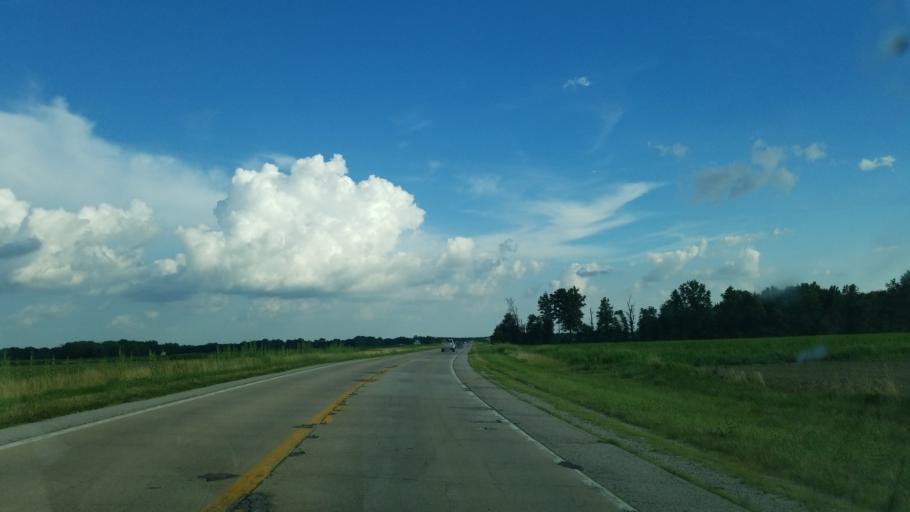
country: US
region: Illinois
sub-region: Marion County
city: Sandoval
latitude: 38.6003
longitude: -89.1084
